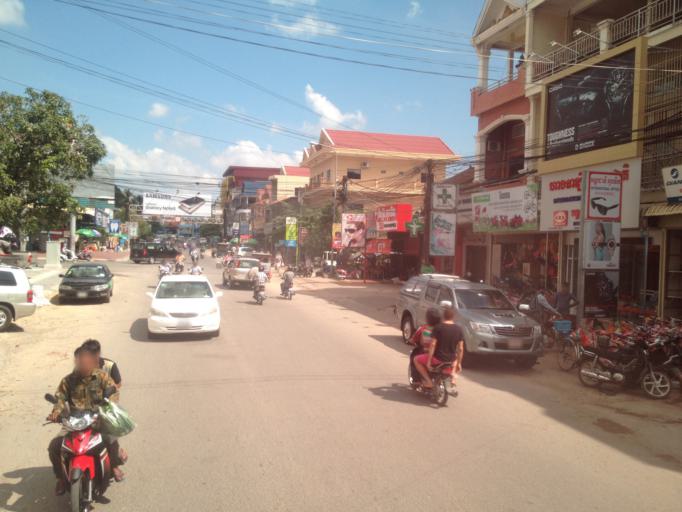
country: KH
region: Preah Sihanouk
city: Sihanoukville
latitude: 10.6217
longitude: 103.5273
